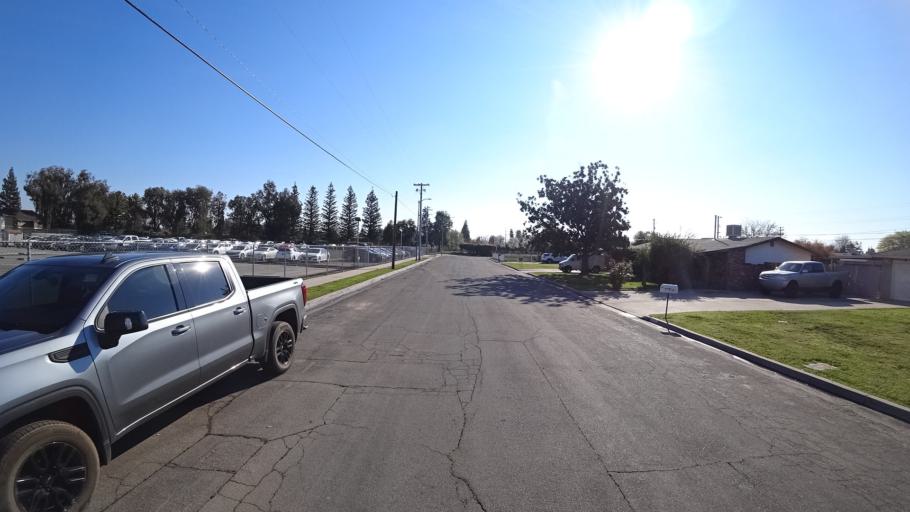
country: US
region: California
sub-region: Fresno County
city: Fresno
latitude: 36.8266
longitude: -119.7868
